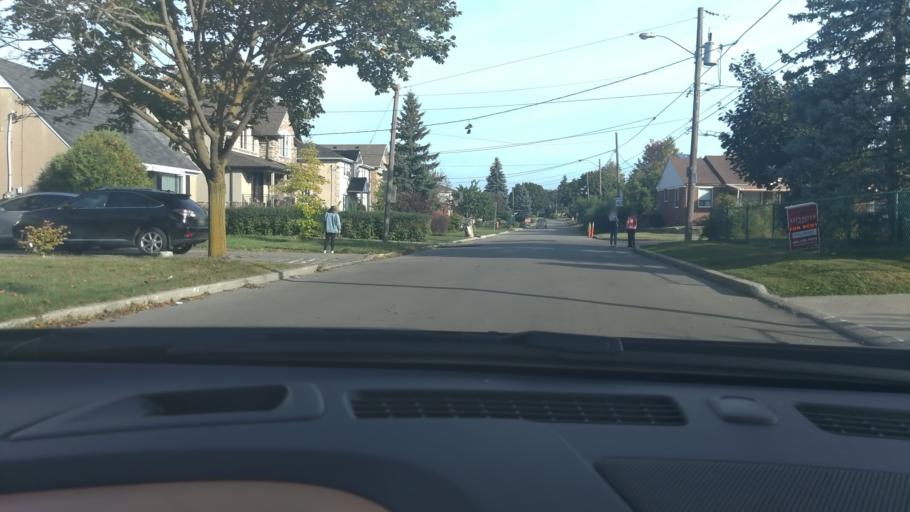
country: CA
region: Ontario
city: Toronto
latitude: 43.7184
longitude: -79.4544
